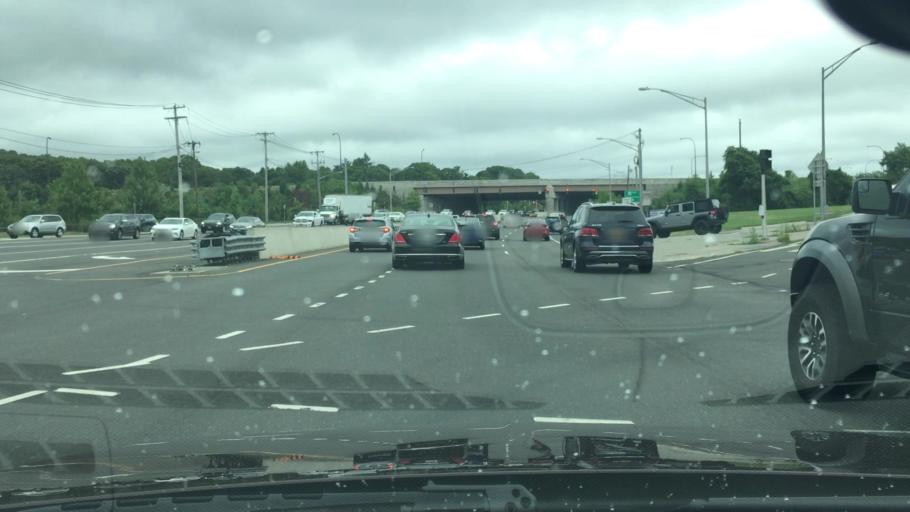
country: US
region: New York
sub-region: Suffolk County
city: Melville
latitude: 40.7940
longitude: -73.4151
